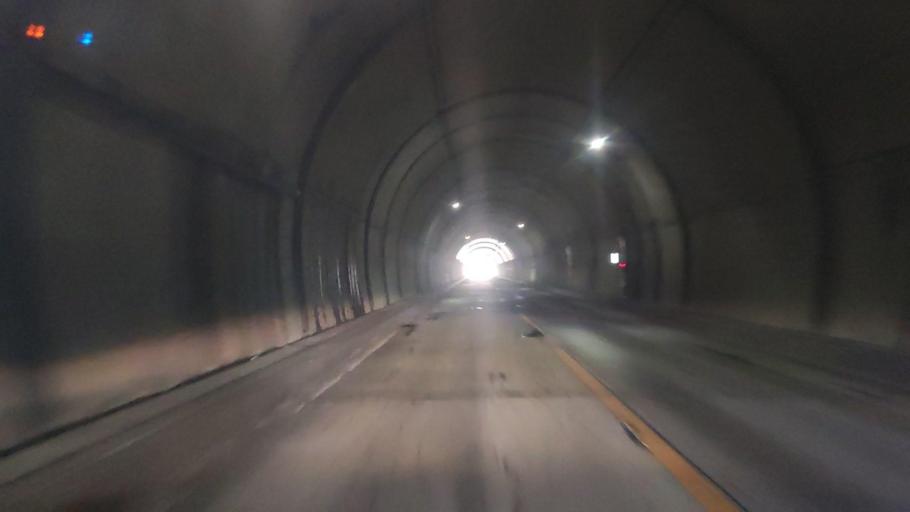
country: JP
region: Oita
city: Saiki
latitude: 32.8846
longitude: 131.9456
